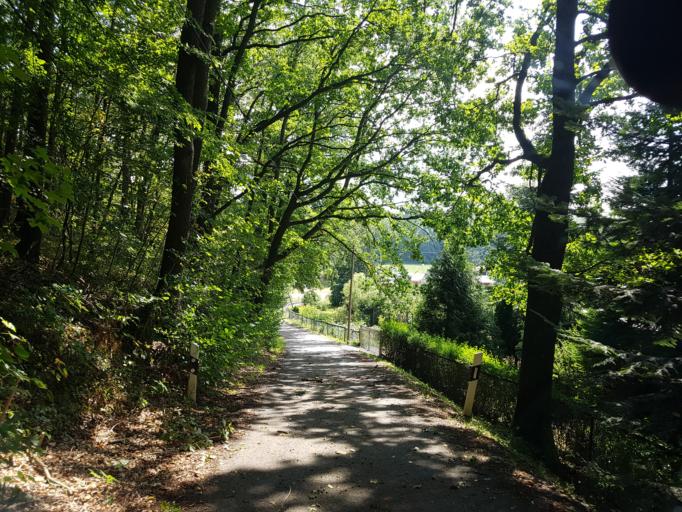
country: DE
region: Saxony
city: Waldheim
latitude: 51.0634
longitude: 13.0078
